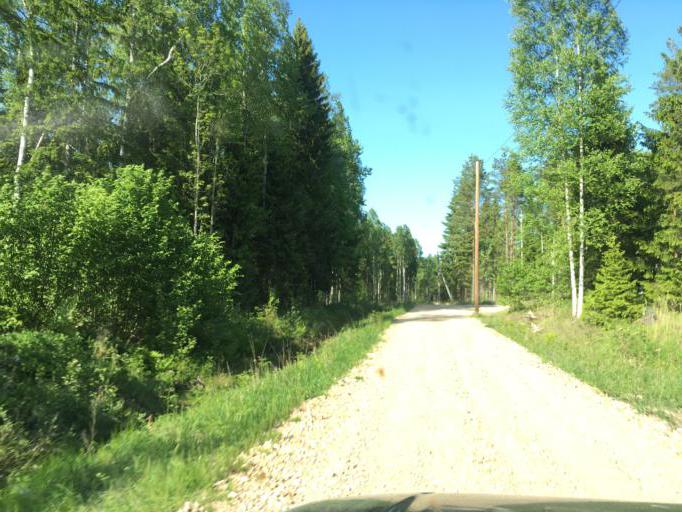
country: LV
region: Dundaga
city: Dundaga
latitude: 57.6048
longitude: 22.5111
